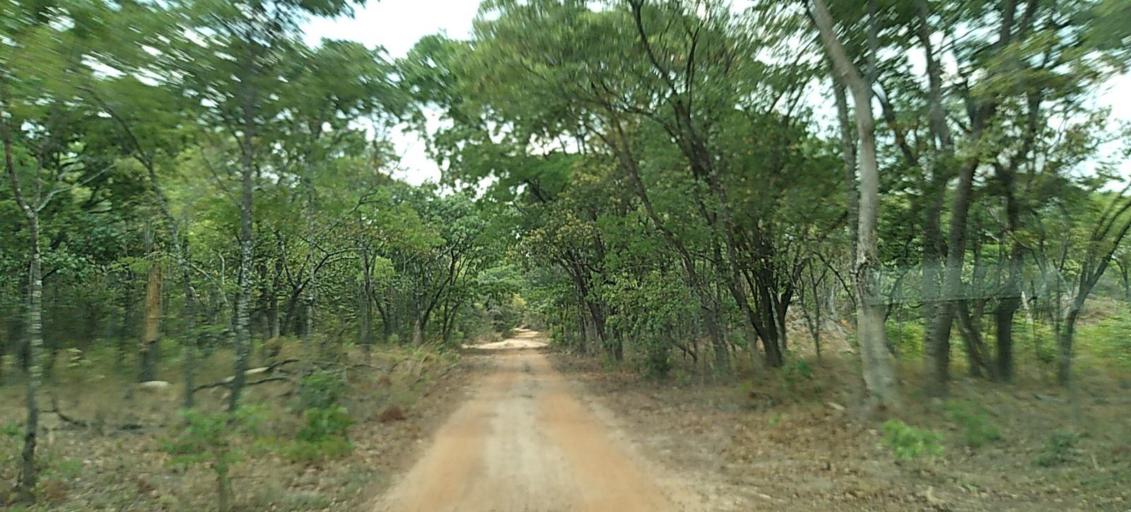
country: ZM
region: Copperbelt
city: Chingola
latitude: -12.7711
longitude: 27.6878
